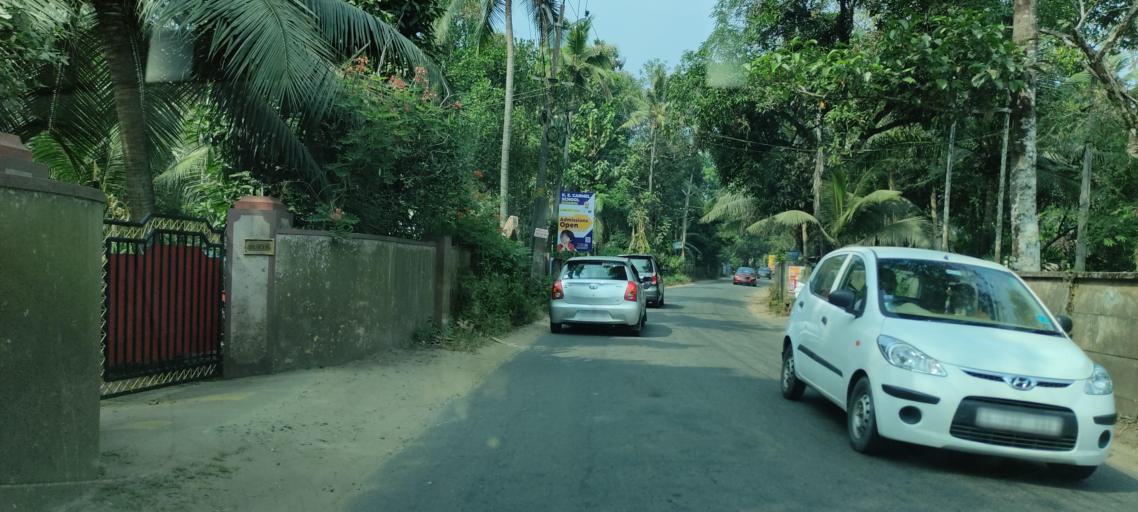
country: IN
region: Kerala
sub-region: Alappuzha
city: Shertallai
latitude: 9.6752
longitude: 76.4211
